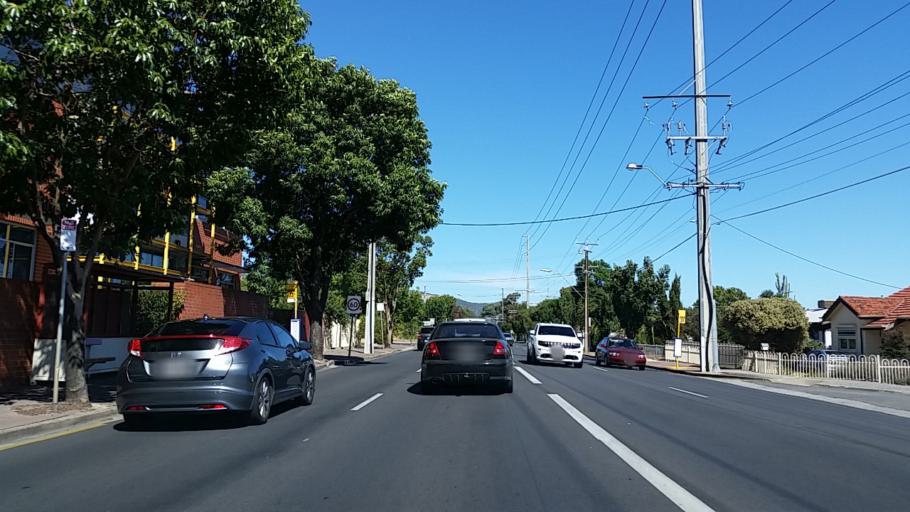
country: AU
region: South Australia
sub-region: Campbelltown
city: Campbelltown
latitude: -34.8824
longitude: 138.6738
